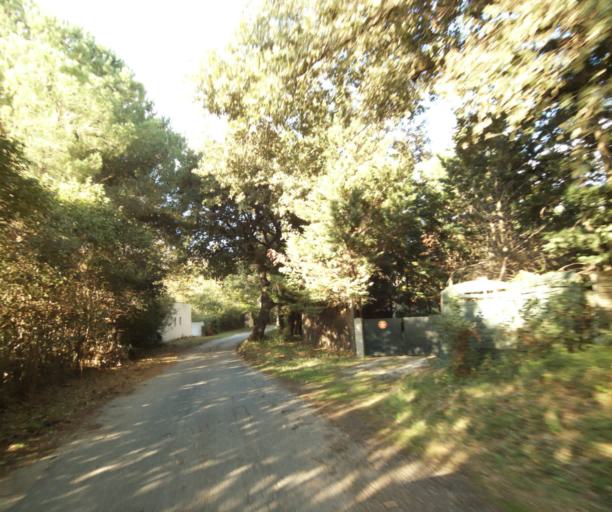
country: FR
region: Languedoc-Roussillon
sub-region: Departement des Pyrenees-Orientales
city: Argelers
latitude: 42.5656
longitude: 3.0131
